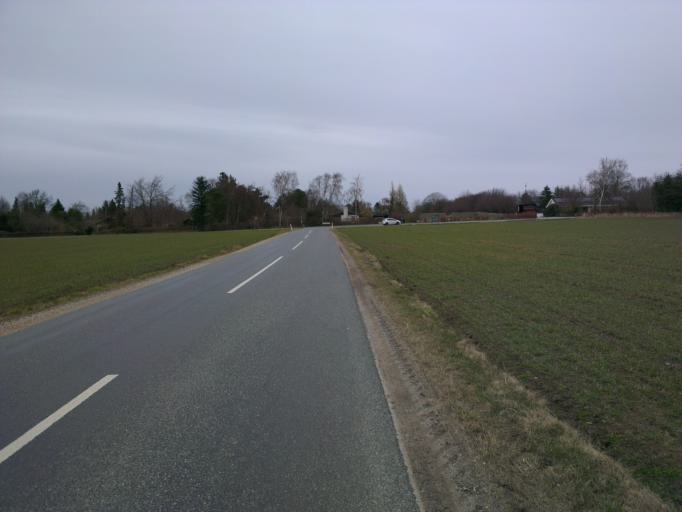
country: DK
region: Capital Region
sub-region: Frederikssund Kommune
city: Jaegerspris
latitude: 55.8268
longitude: 11.9621
